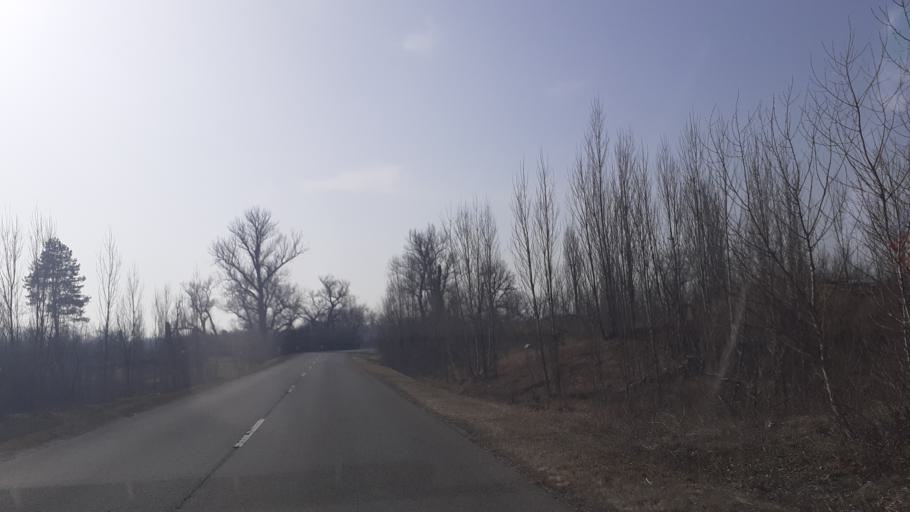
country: HU
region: Pest
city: Orkeny
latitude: 47.1029
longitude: 19.3941
